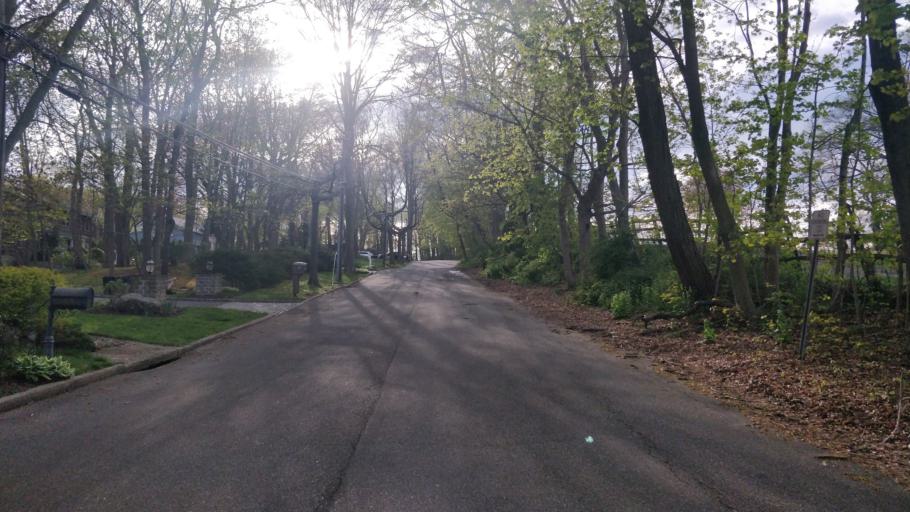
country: US
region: New York
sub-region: Suffolk County
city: Fort Salonga
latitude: 40.9167
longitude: -73.3016
